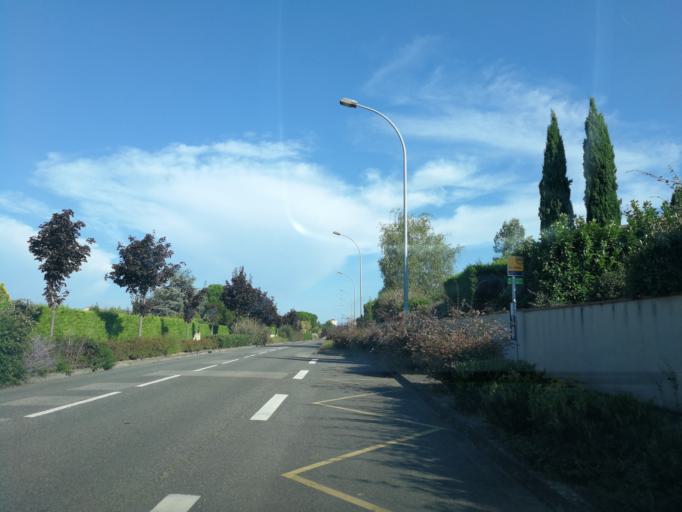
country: FR
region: Midi-Pyrenees
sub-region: Departement de la Haute-Garonne
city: Balma
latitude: 43.6202
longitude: 1.5148
